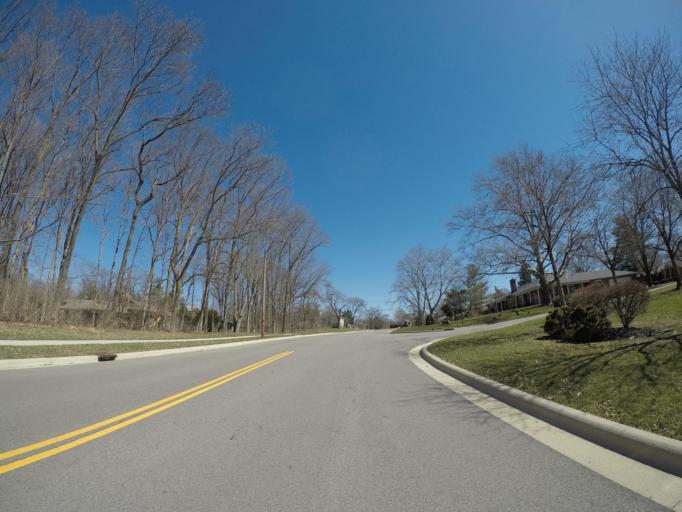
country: US
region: Ohio
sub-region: Franklin County
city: Upper Arlington
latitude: 40.0131
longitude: -83.0854
